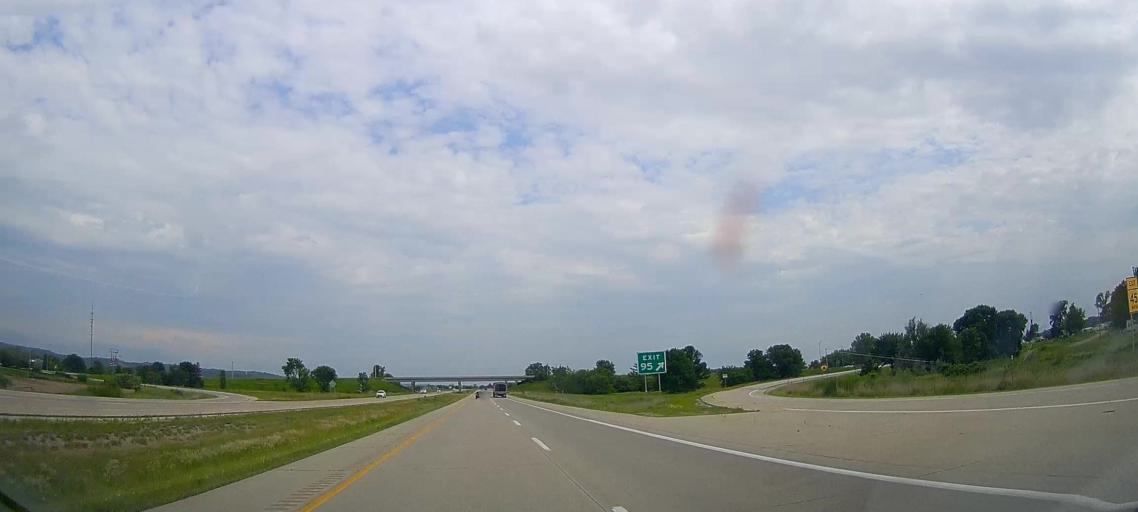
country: US
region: Nebraska
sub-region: Burt County
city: Tekamah
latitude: 41.8039
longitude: -96.0578
